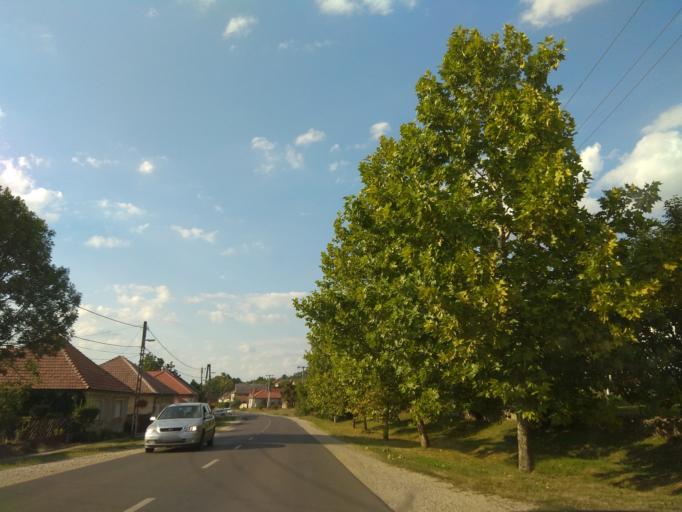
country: HU
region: Borsod-Abauj-Zemplen
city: Harsany
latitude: 47.9615
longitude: 20.7438
